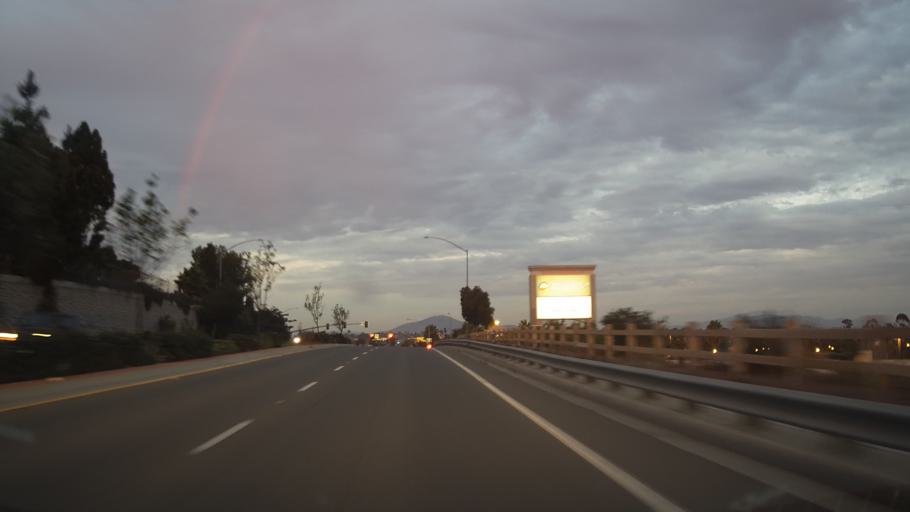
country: US
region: California
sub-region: San Diego County
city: National City
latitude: 32.7041
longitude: -117.1036
